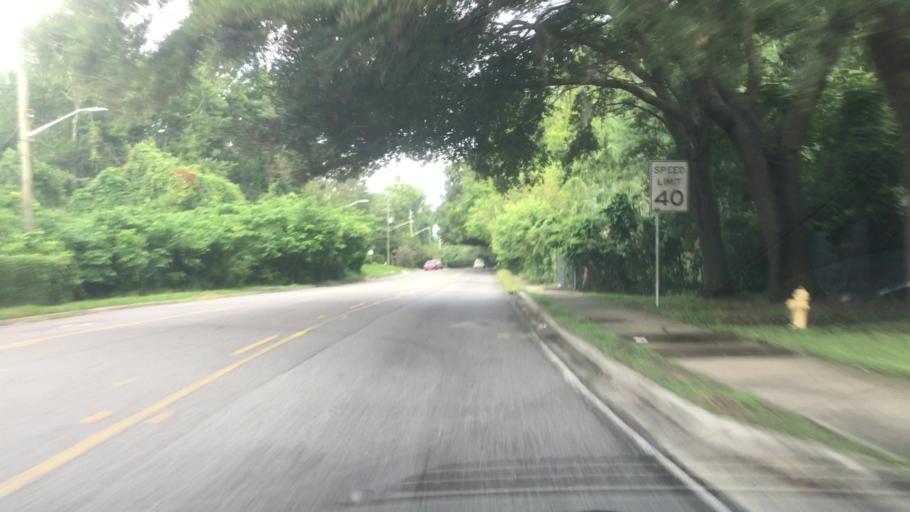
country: US
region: Florida
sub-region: Duval County
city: Jacksonville
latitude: 30.2937
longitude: -81.6107
